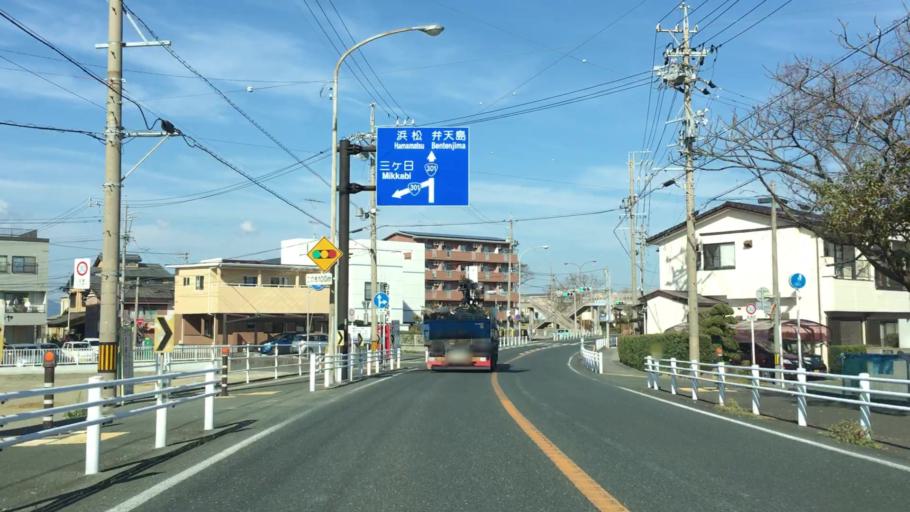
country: JP
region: Shizuoka
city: Kosai-shi
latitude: 34.6927
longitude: 137.5651
